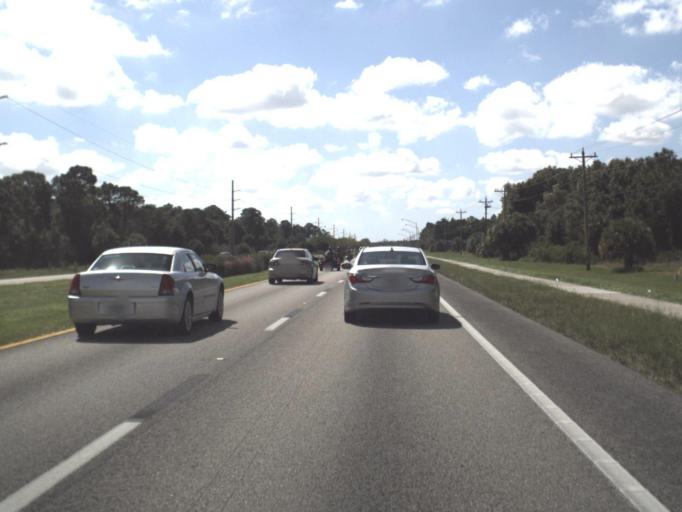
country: US
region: Florida
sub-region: Lee County
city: Palmona Park
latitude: 26.6947
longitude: -81.9010
